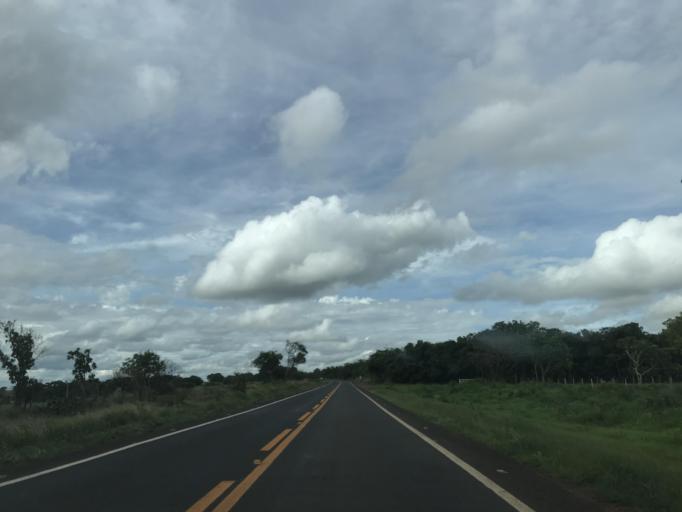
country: BR
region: Goias
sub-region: Piracanjuba
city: Piracanjuba
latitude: -17.3985
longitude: -48.8049
